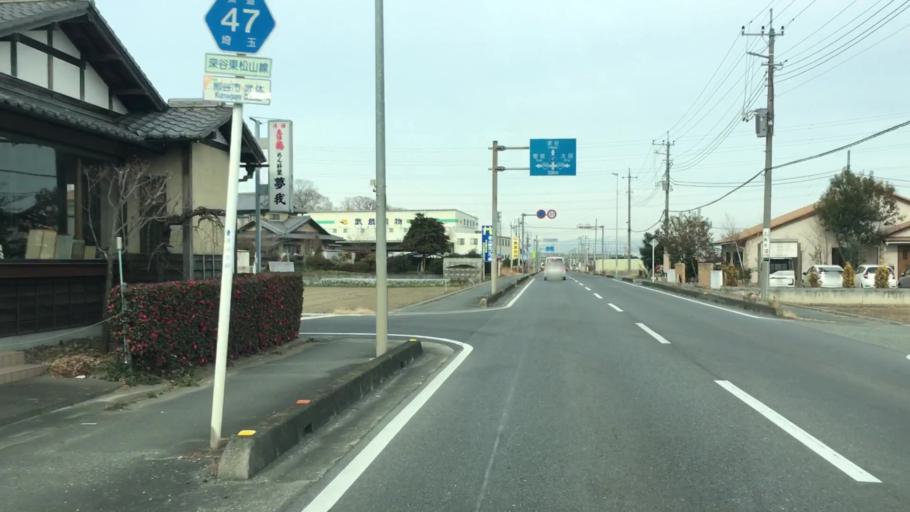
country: JP
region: Saitama
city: Fukayacho
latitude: 36.1471
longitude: 139.3227
